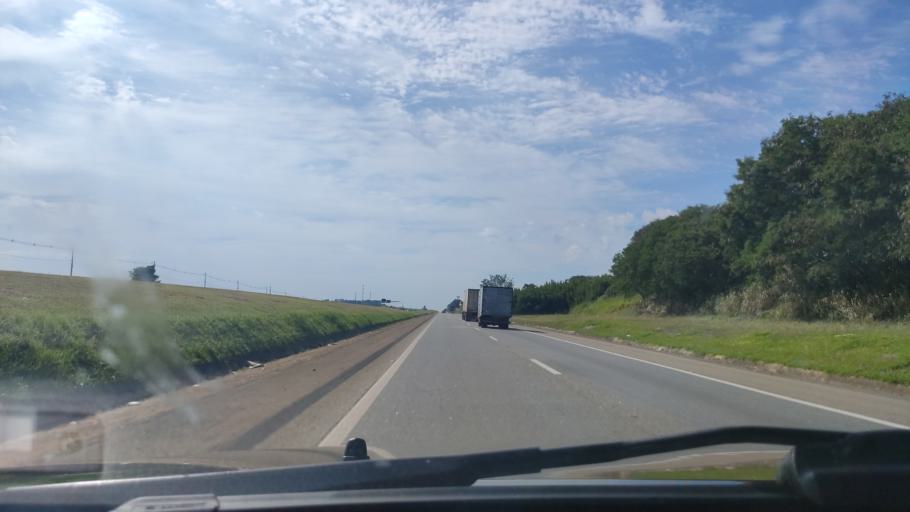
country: BR
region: Sao Paulo
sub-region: Boituva
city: Boituva
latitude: -23.3182
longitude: -47.6261
